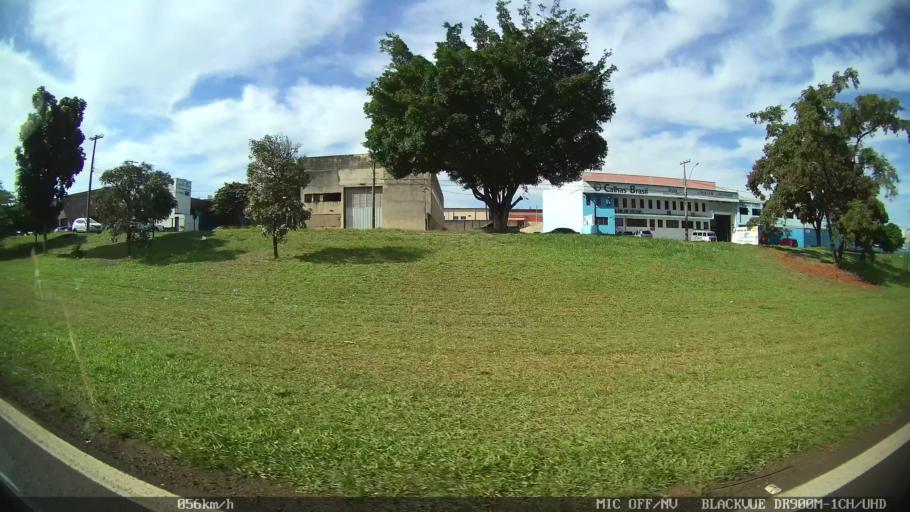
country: BR
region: Sao Paulo
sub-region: Araraquara
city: Araraquara
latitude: -21.8209
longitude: -48.1561
